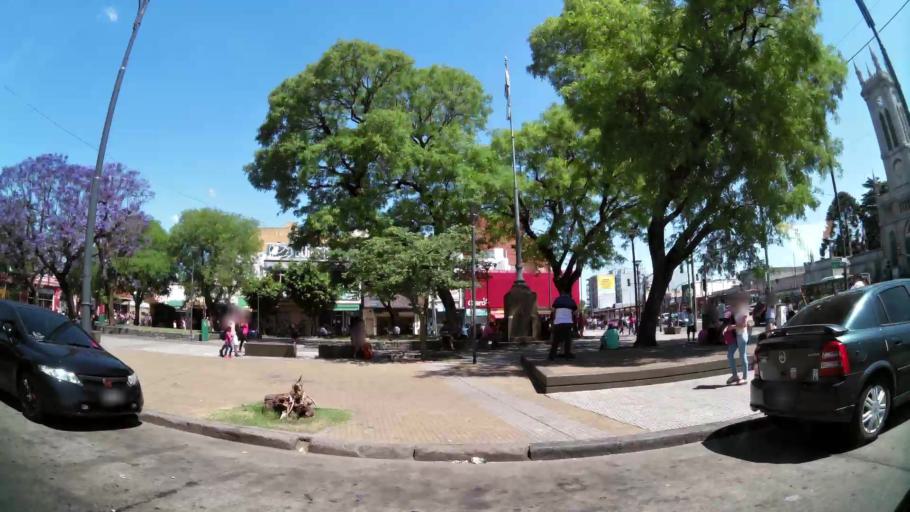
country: AR
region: Buenos Aires
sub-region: Partido de Avellaneda
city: Avellaneda
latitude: -34.6518
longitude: -58.4160
